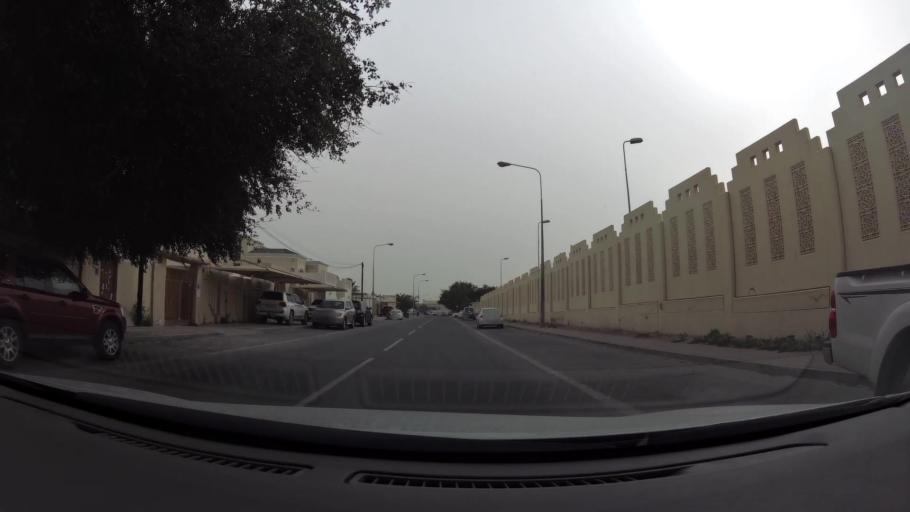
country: QA
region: Baladiyat ad Dawhah
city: Doha
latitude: 25.2553
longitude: 51.5020
